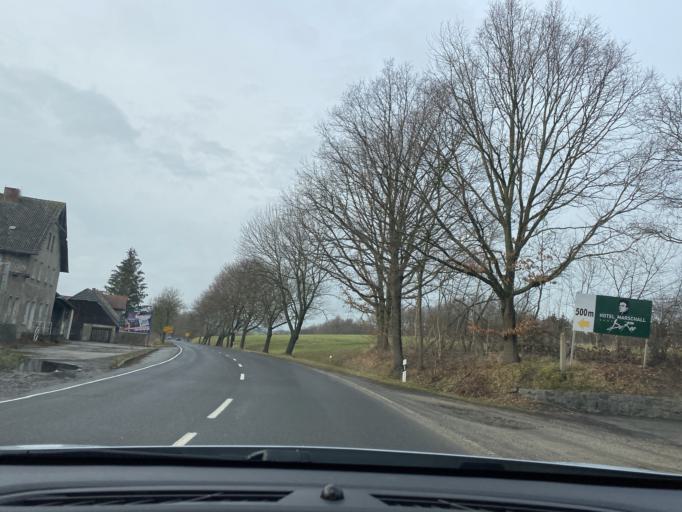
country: DE
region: Saxony
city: Markersdorf
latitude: 51.1460
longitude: 14.9204
